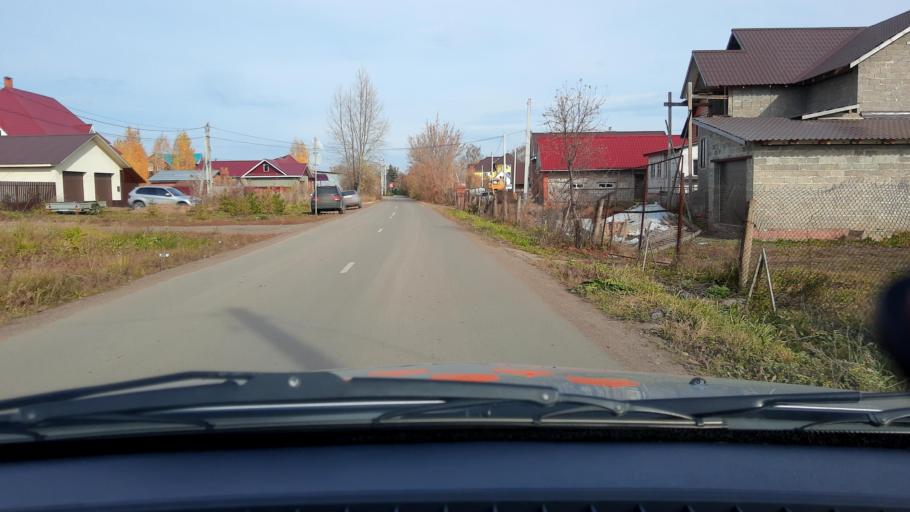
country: RU
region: Bashkortostan
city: Mikhaylovka
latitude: 54.7884
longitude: 55.8295
